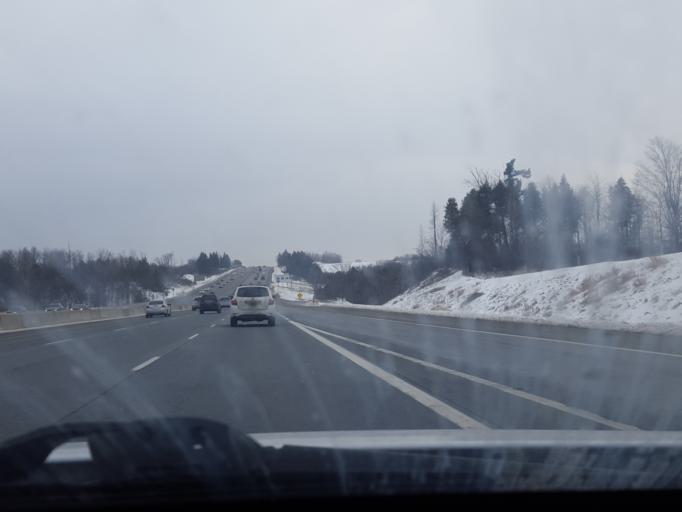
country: CA
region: Ontario
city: Vaughan
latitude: 43.9145
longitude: -79.5649
